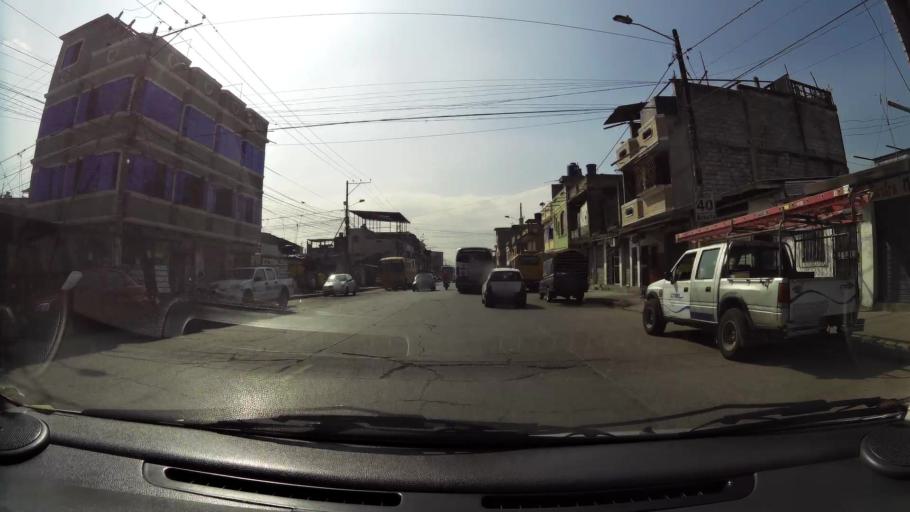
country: EC
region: Guayas
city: Eloy Alfaro
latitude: -2.1688
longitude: -79.7991
